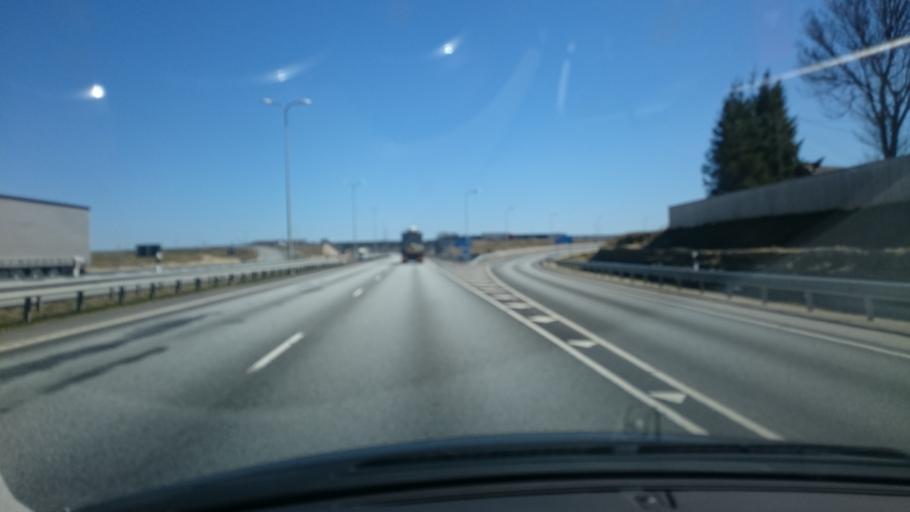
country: EE
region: Harju
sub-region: Kiili vald
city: Kiili
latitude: 59.3357
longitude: 24.8181
